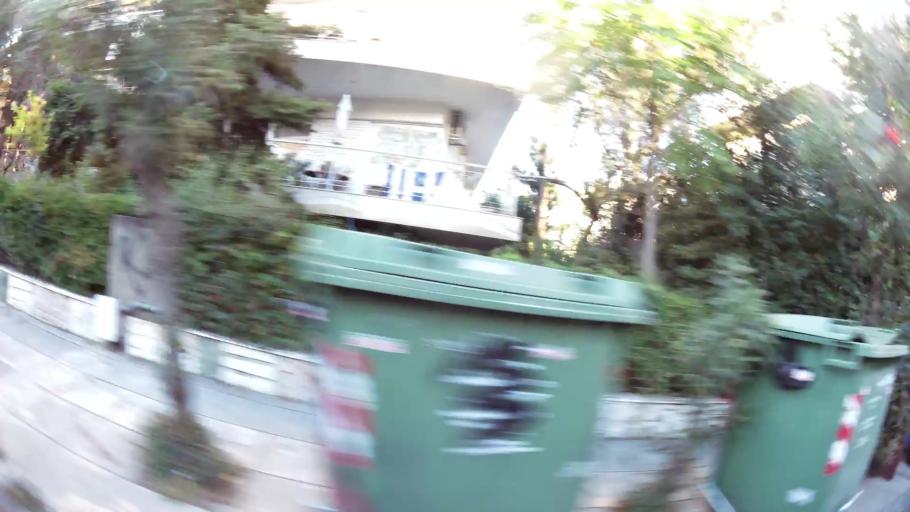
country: GR
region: Attica
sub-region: Nomarchia Athinas
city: Khalandrion
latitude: 38.0163
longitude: 23.8006
